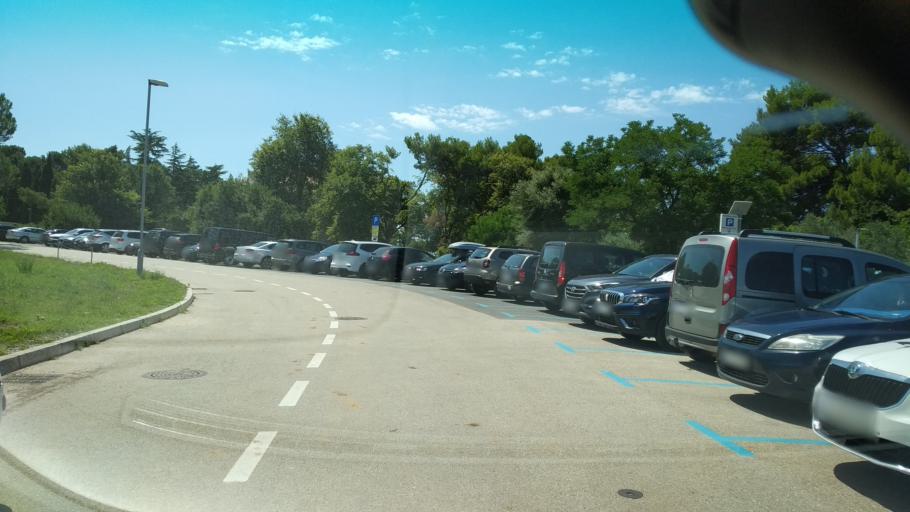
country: HR
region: Istarska
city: Fazana
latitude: 44.9224
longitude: 13.8026
